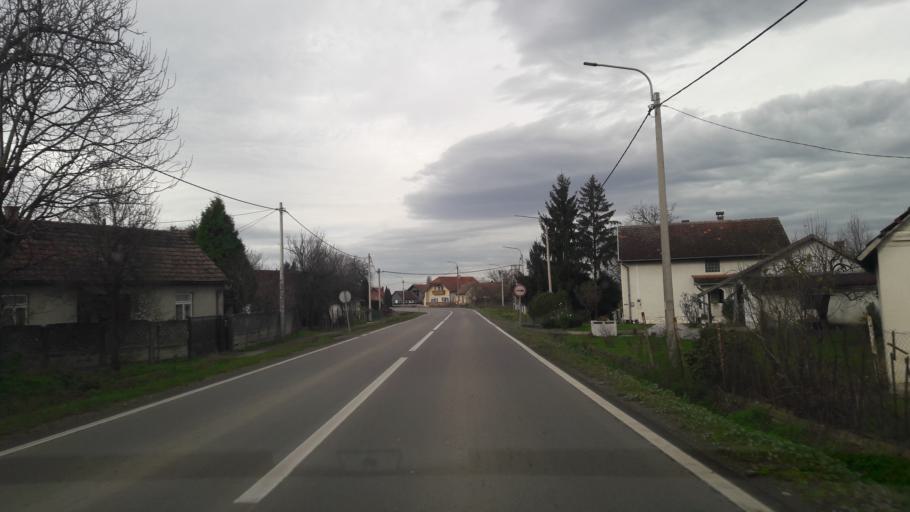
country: HR
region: Osjecko-Baranjska
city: Fericanci
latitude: 45.5227
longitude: 17.9968
